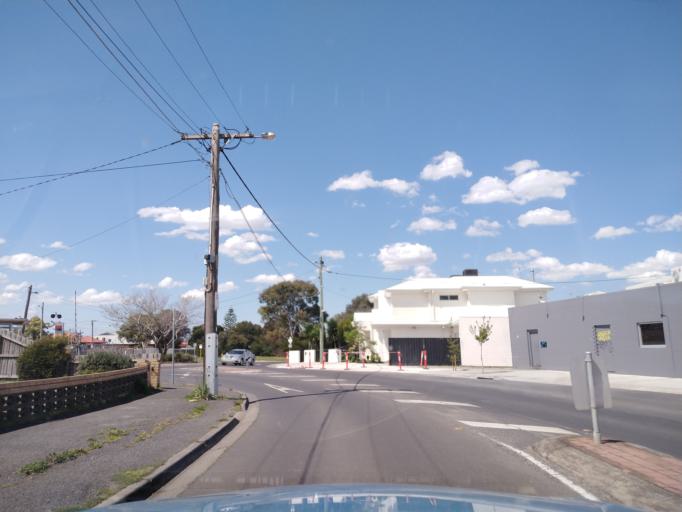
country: AU
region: Victoria
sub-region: Hobsons Bay
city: South Kingsville
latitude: -37.8288
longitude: 144.8721
